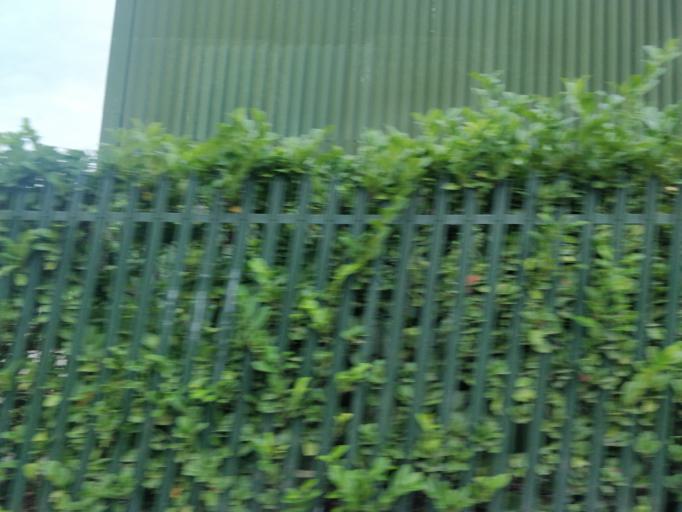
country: GB
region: England
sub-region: Lancashire
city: Ormskirk
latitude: 53.5993
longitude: -2.8655
